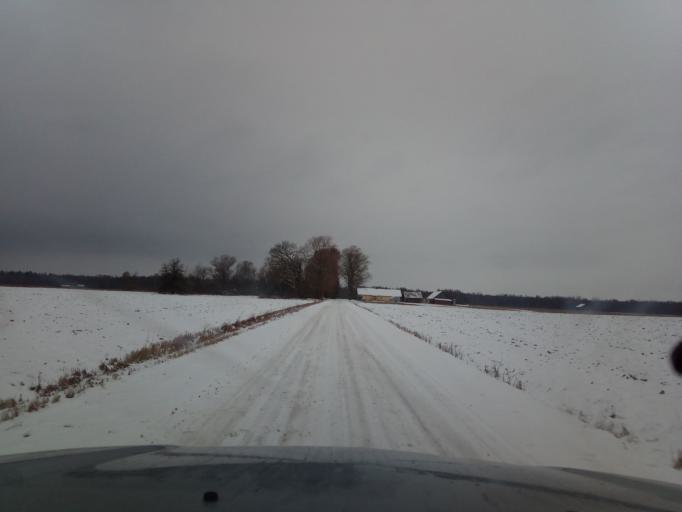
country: LT
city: Ramygala
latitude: 55.4845
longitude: 24.5756
